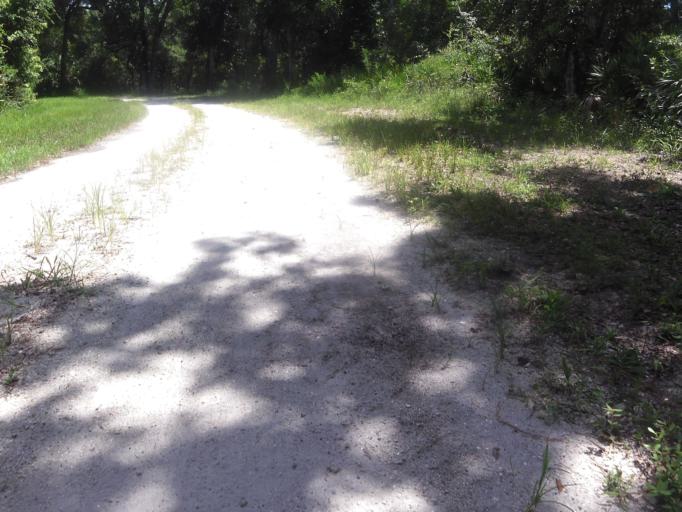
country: US
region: Florida
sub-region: Saint Johns County
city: Villano Beach
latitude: 30.0432
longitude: -81.3379
